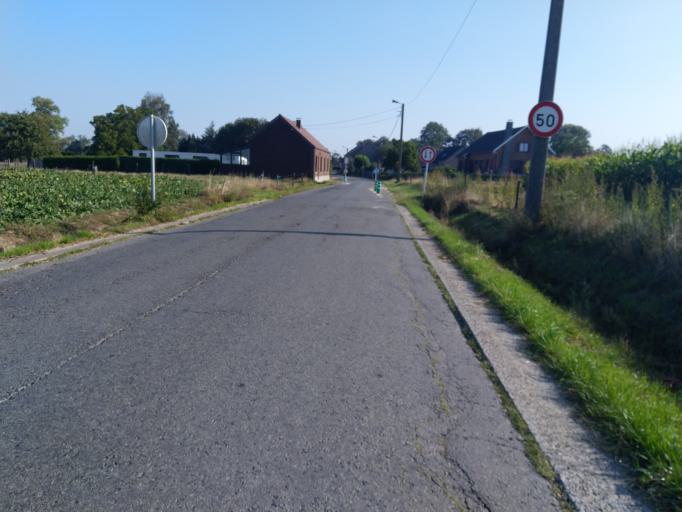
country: BE
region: Wallonia
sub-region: Province du Hainaut
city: Soignies
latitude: 50.5421
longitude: 4.0881
